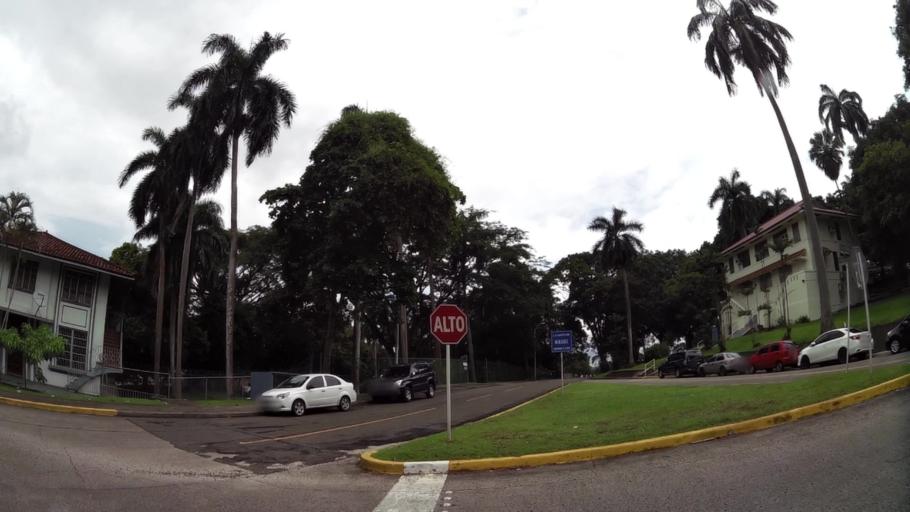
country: PA
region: Panama
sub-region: Distrito de Panama
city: Ancon
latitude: 8.9611
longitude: -79.5541
